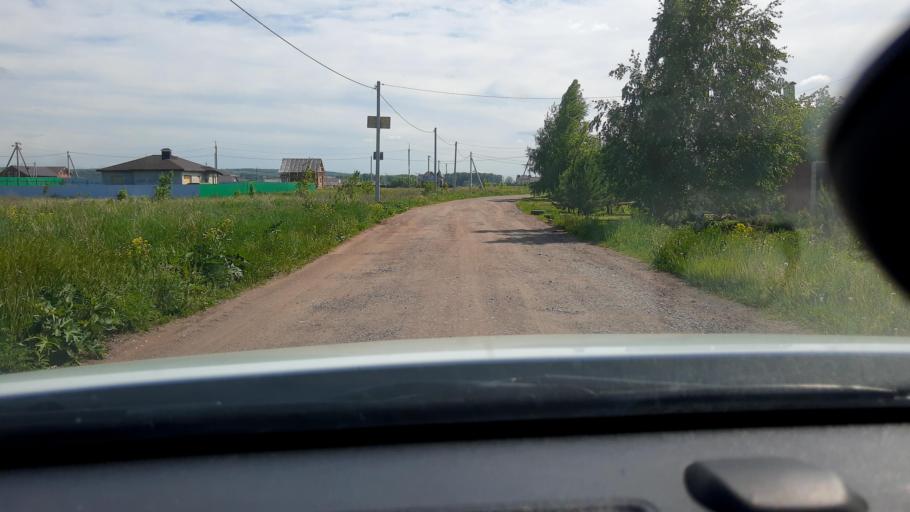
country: RU
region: Bashkortostan
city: Avdon
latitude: 54.4471
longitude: 55.8191
